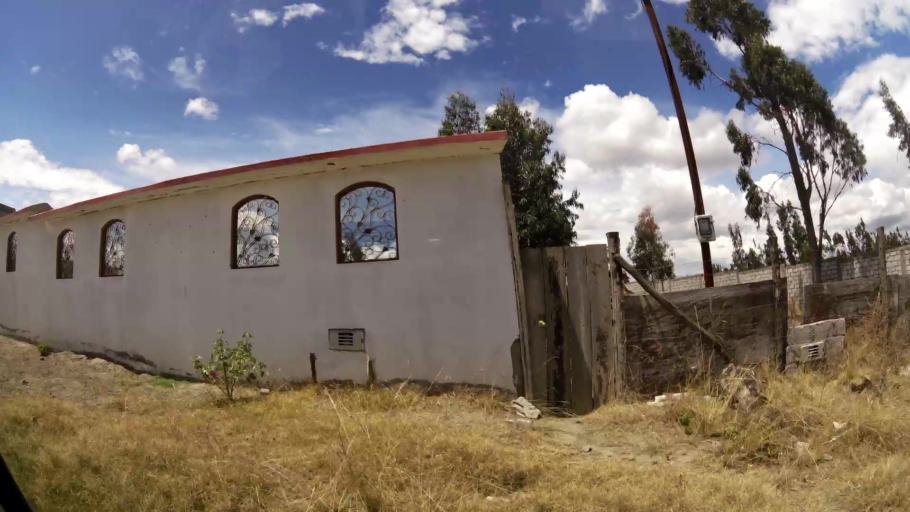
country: EC
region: Tungurahua
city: Ambato
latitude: -1.2799
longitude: -78.5984
